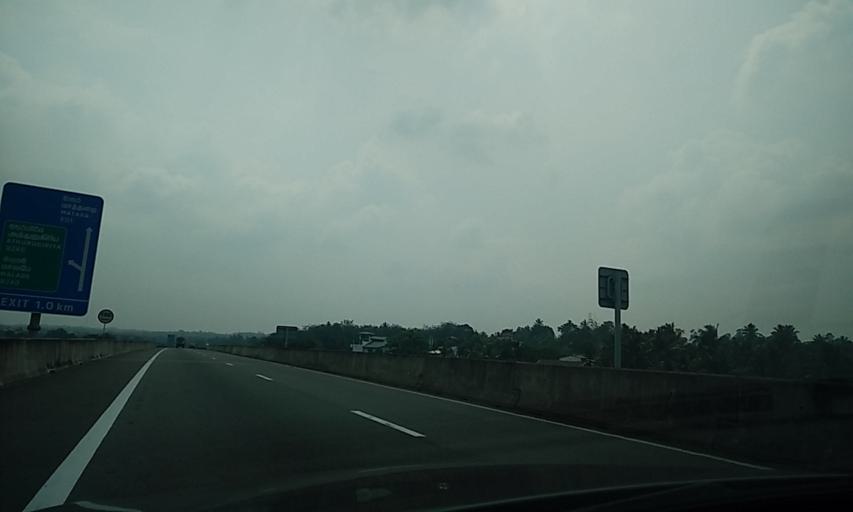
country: LK
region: Western
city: Homagama
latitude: 6.8948
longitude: 79.9786
